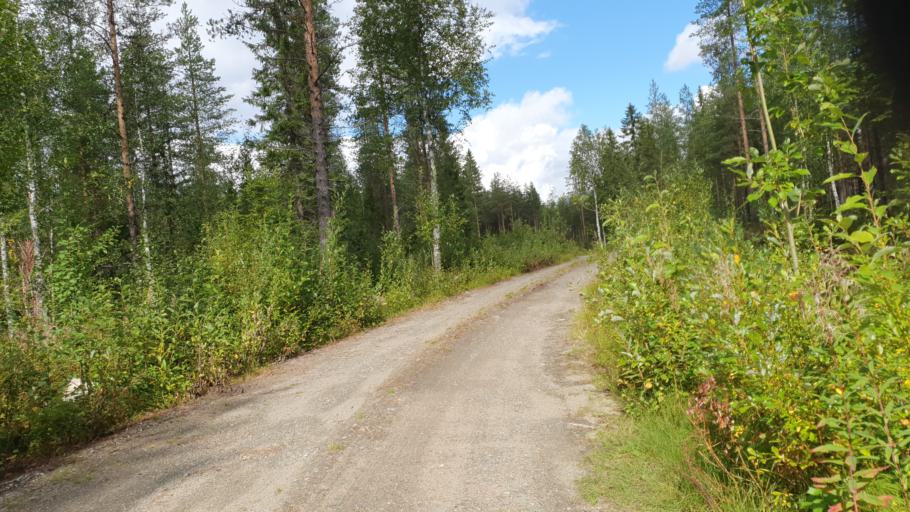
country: FI
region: Kainuu
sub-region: Kehys-Kainuu
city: Kuhmo
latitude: 64.1410
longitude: 29.3871
